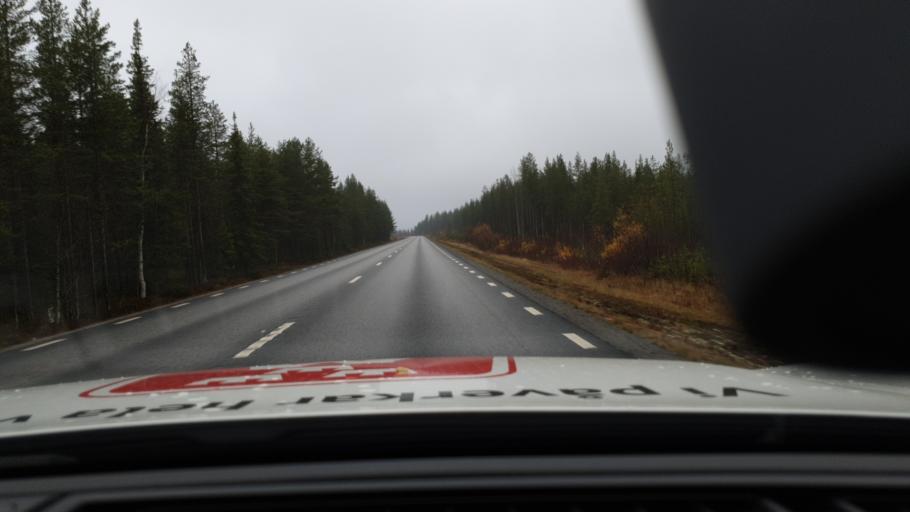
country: SE
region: Norrbotten
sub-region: Overkalix Kommun
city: OEverkalix
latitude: 66.6160
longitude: 22.2359
